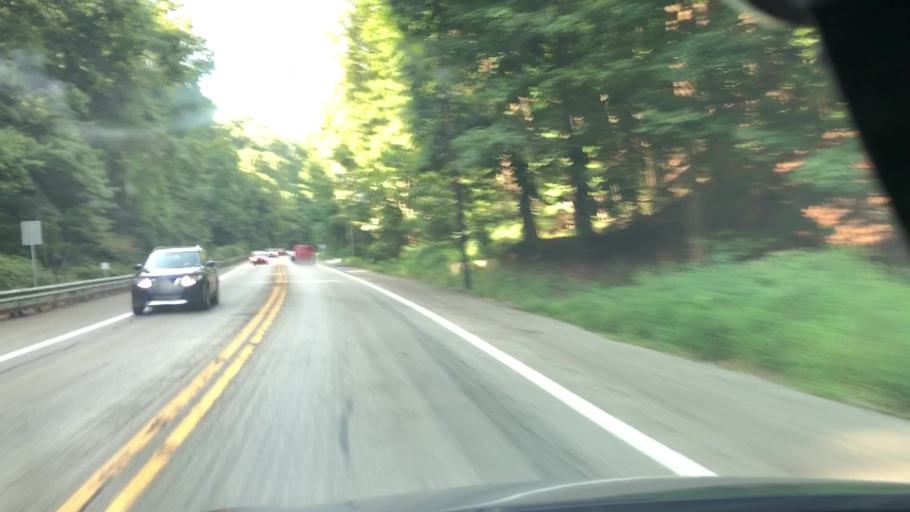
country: US
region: Pennsylvania
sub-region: Allegheny County
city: Pitcairn
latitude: 40.4087
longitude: -79.7610
